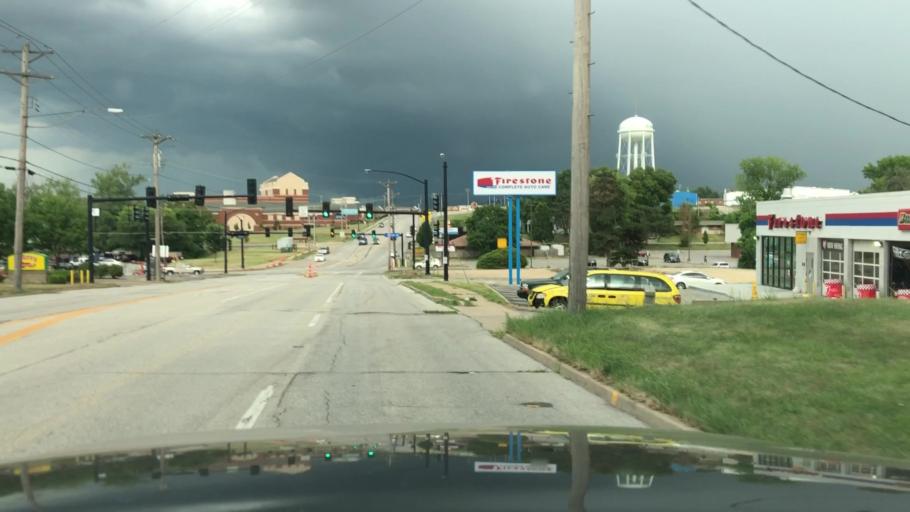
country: US
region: Missouri
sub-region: Saint Charles County
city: Saint Charles
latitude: 38.7839
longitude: -90.5110
